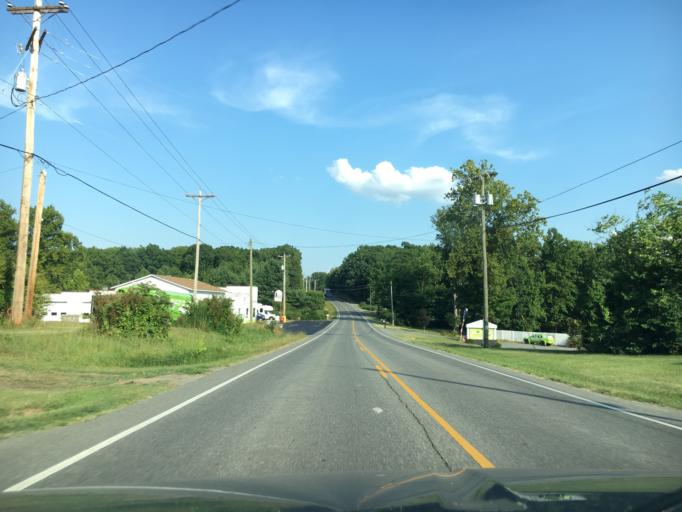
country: US
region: Virginia
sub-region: Franklin County
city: Union Hall
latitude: 37.0073
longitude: -79.7784
